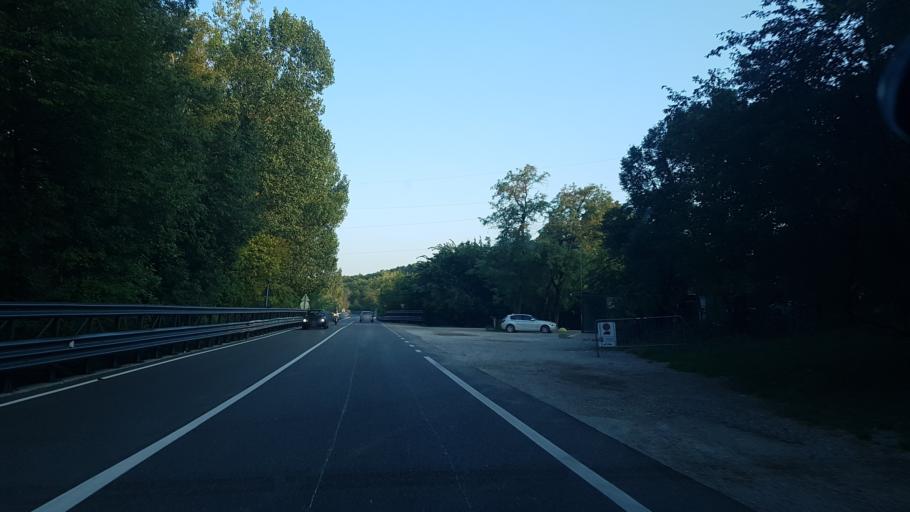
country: IT
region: Friuli Venezia Giulia
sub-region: Provincia di Trieste
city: Duino
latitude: 45.7947
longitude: 13.5835
